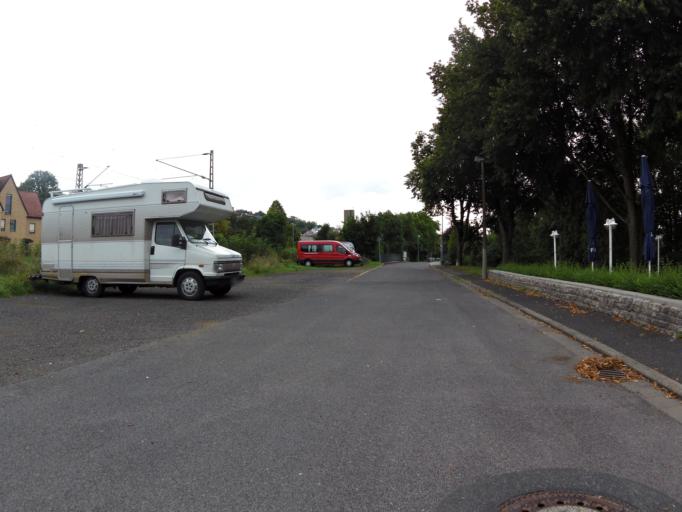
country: DE
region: Bavaria
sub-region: Regierungsbezirk Unterfranken
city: Schonungen
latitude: 50.0505
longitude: 10.3021
